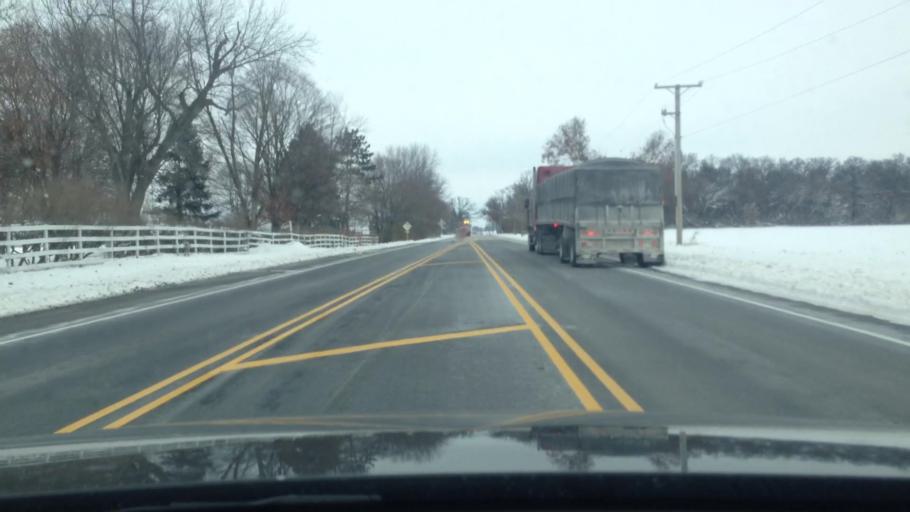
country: US
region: Illinois
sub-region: McHenry County
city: Hebron
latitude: 42.4155
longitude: -88.4381
